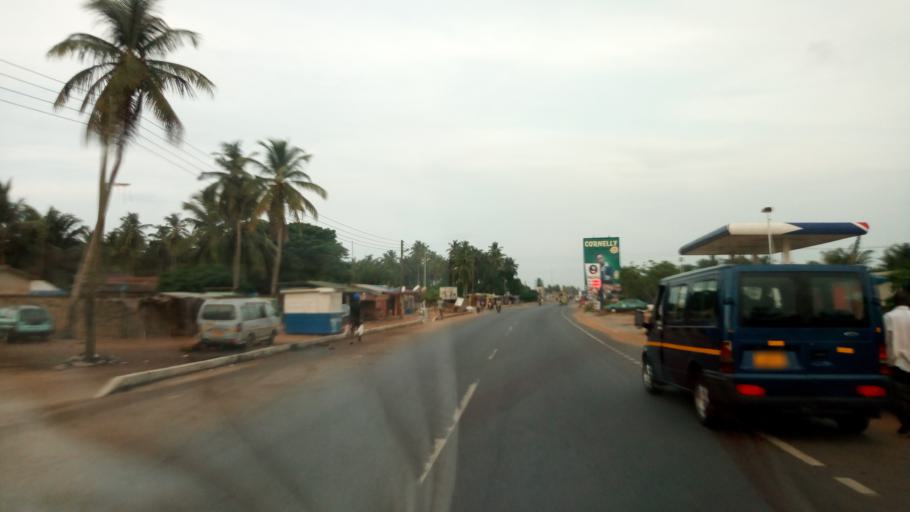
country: TG
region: Maritime
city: Lome
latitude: 6.1144
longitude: 1.1682
